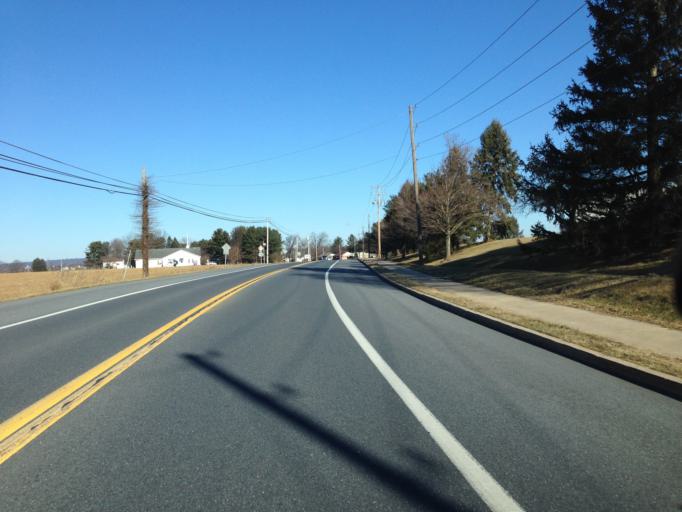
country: US
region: Pennsylvania
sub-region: Lancaster County
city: Lititz
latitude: 40.1637
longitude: -76.3180
